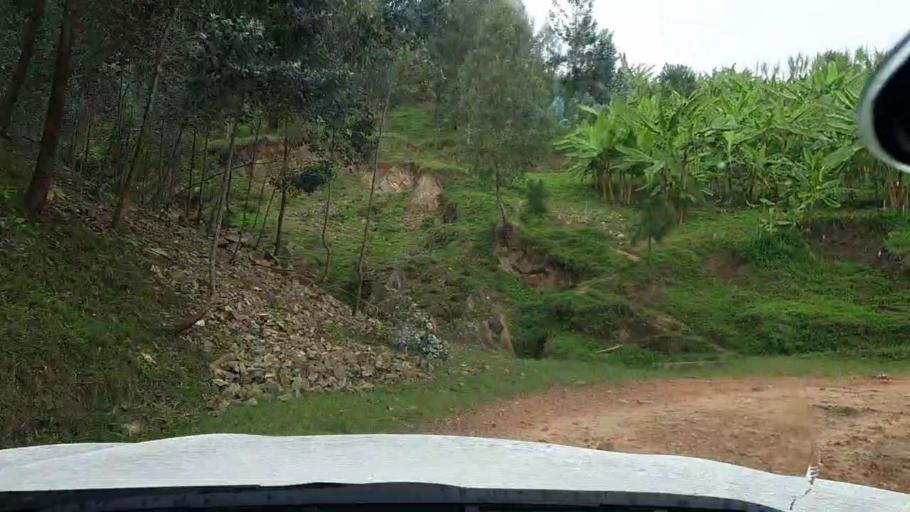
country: RW
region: Western Province
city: Kibuye
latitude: -2.0769
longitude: 29.4445
